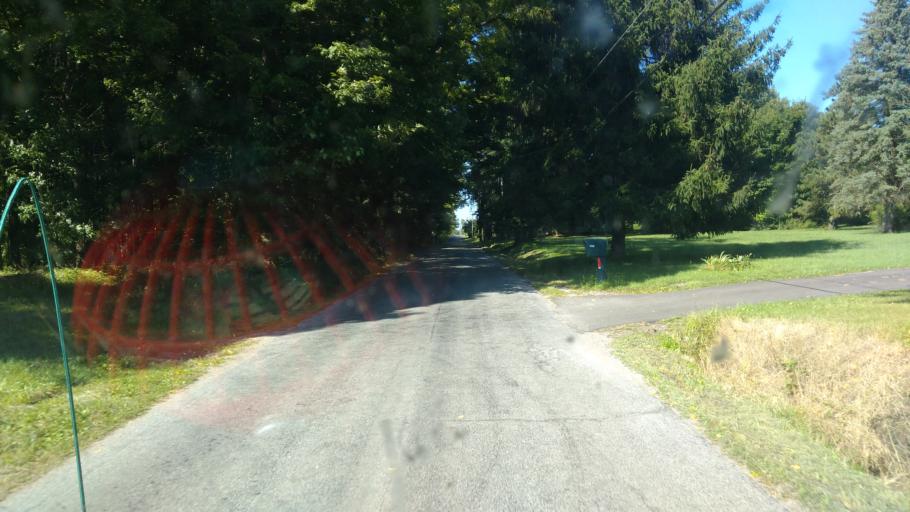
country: US
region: Ohio
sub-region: Ashland County
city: Ashland
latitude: 40.8928
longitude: -82.2688
